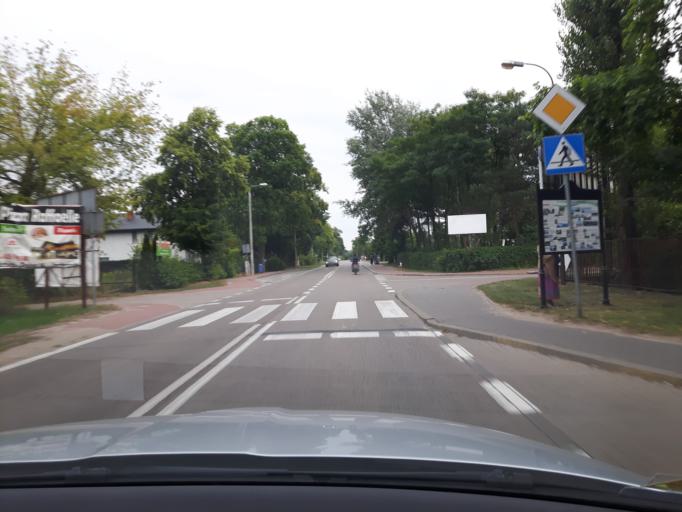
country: PL
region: Masovian Voivodeship
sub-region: Powiat legionowski
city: Wieliszew
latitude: 52.4866
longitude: 20.9694
